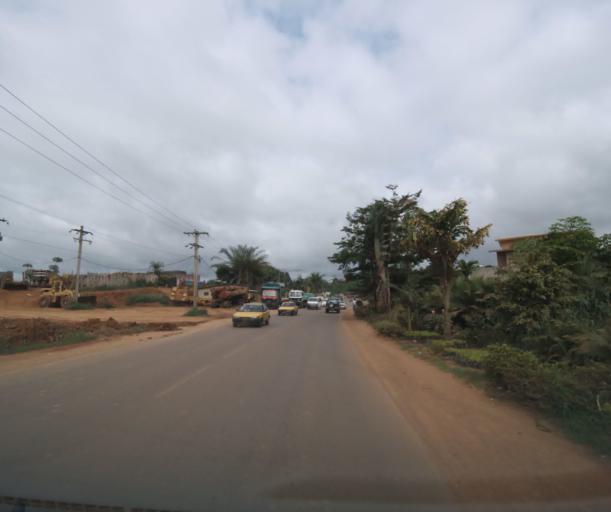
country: CM
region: Centre
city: Yaounde
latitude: 3.8022
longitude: 11.5090
